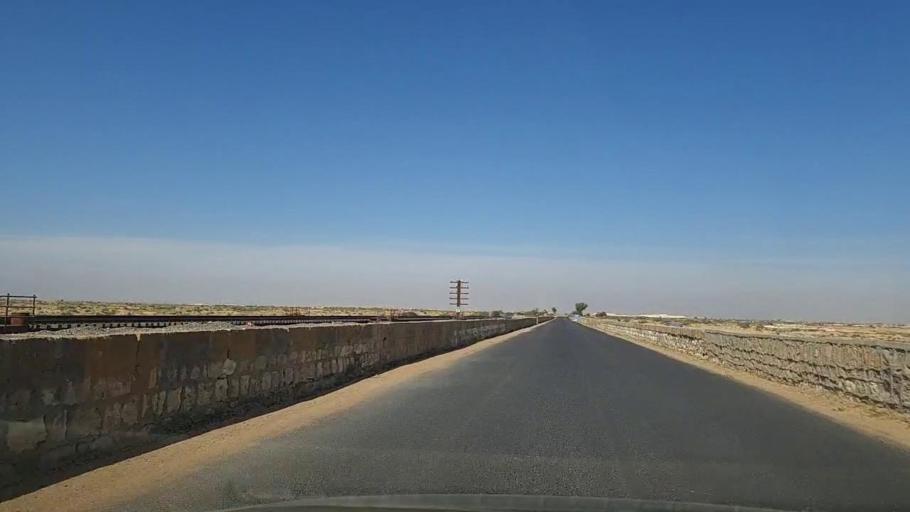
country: PK
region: Sindh
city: Kotri
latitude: 25.2982
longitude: 68.2036
